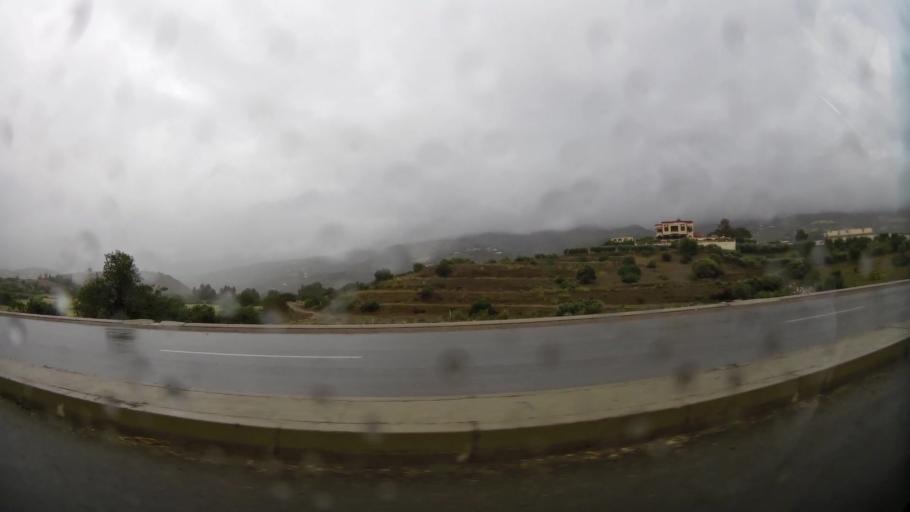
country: MA
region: Taza-Al Hoceima-Taounate
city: Imzourene
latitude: 35.0407
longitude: -3.8217
